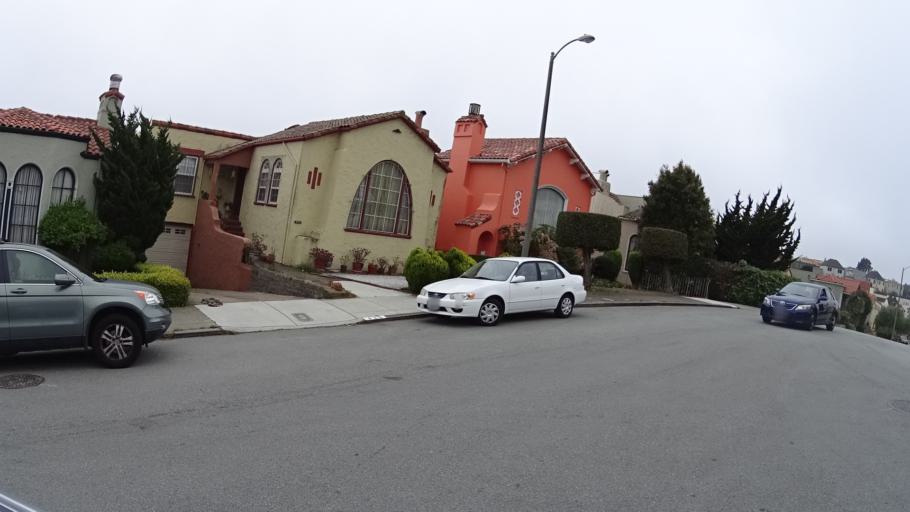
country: US
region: California
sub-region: San Mateo County
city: Daly City
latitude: 37.7345
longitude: -122.4574
